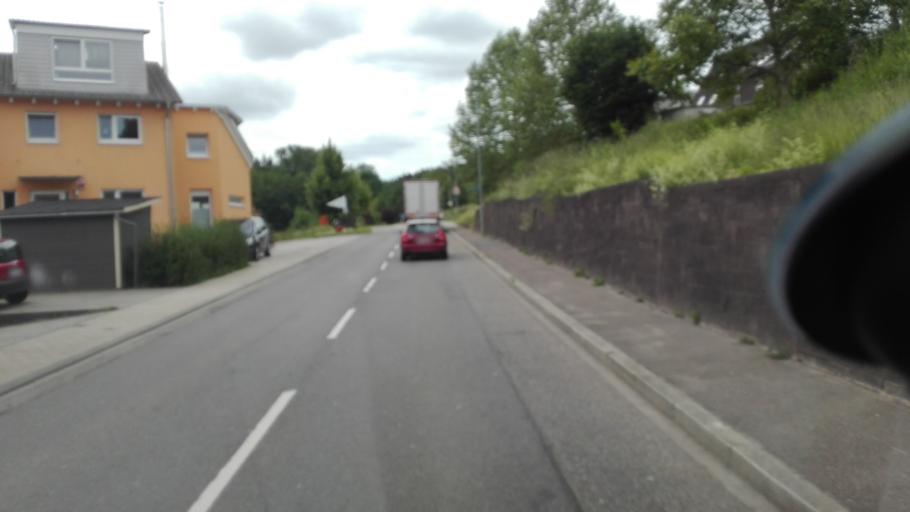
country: DE
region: Baden-Wuerttemberg
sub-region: Karlsruhe Region
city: Konigsbach-Stein
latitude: 48.9629
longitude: 8.5443
